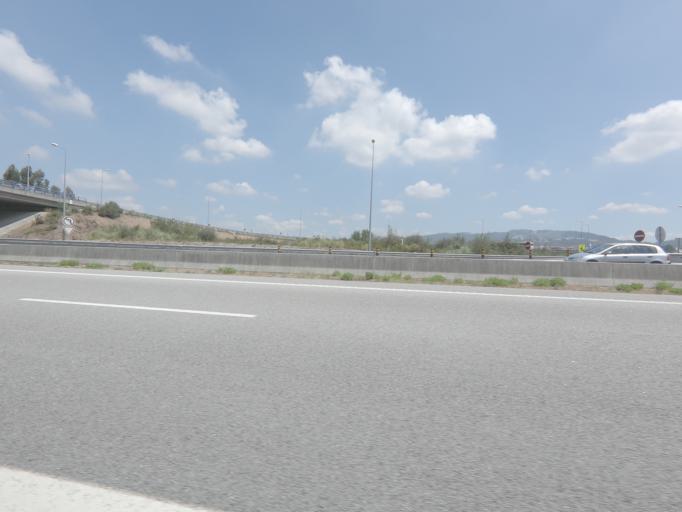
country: PT
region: Porto
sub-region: Valongo
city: Campo
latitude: 41.1795
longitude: -8.4442
